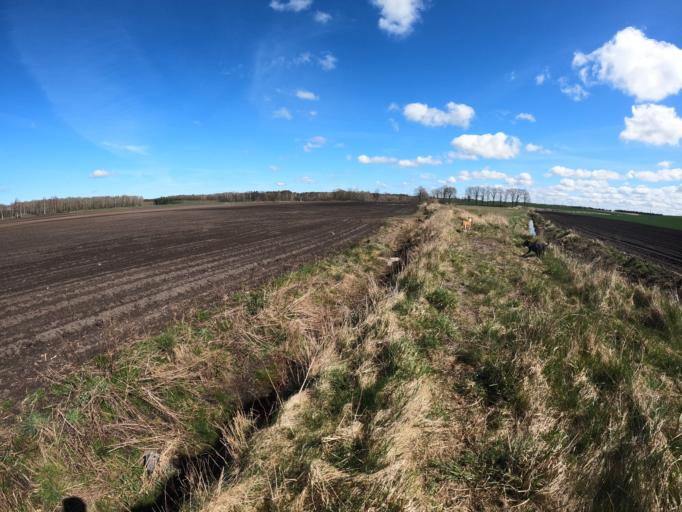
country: PL
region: West Pomeranian Voivodeship
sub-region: Powiat gryficki
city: Gryfice
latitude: 53.9249
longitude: 15.2438
